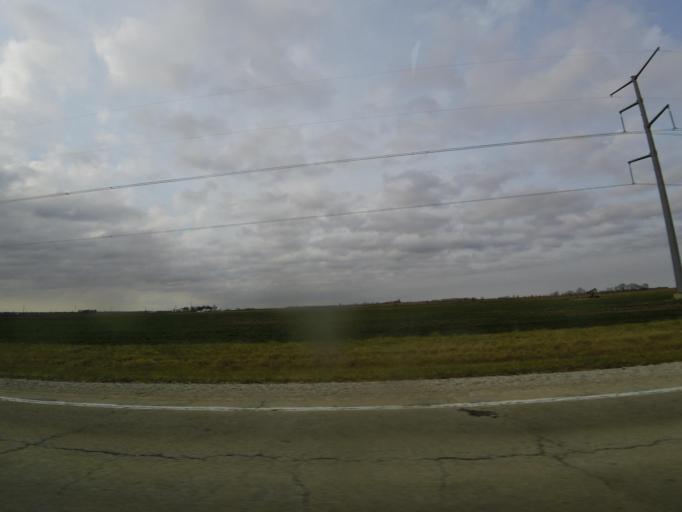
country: US
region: Illinois
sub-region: Christian County
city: Pana
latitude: 39.4247
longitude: -89.0437
